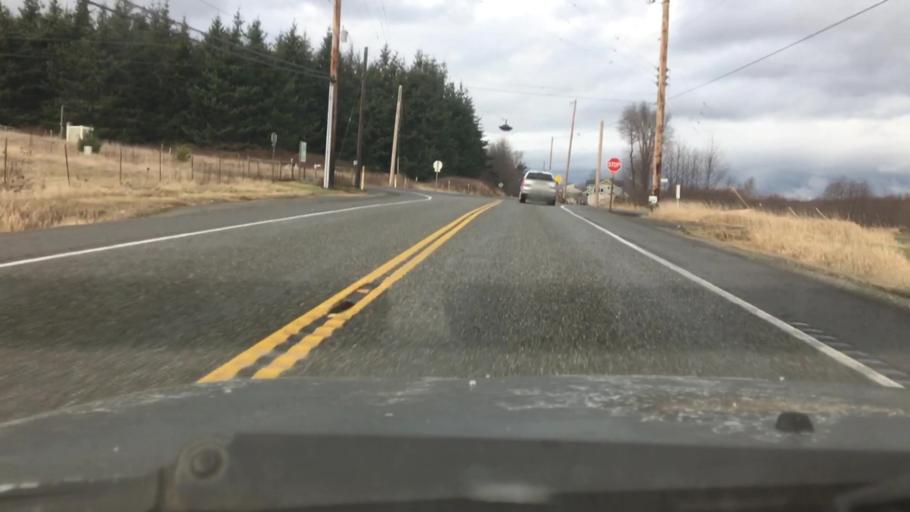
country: US
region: Washington
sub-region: Whatcom County
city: Ferndale
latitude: 48.8479
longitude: -122.6826
